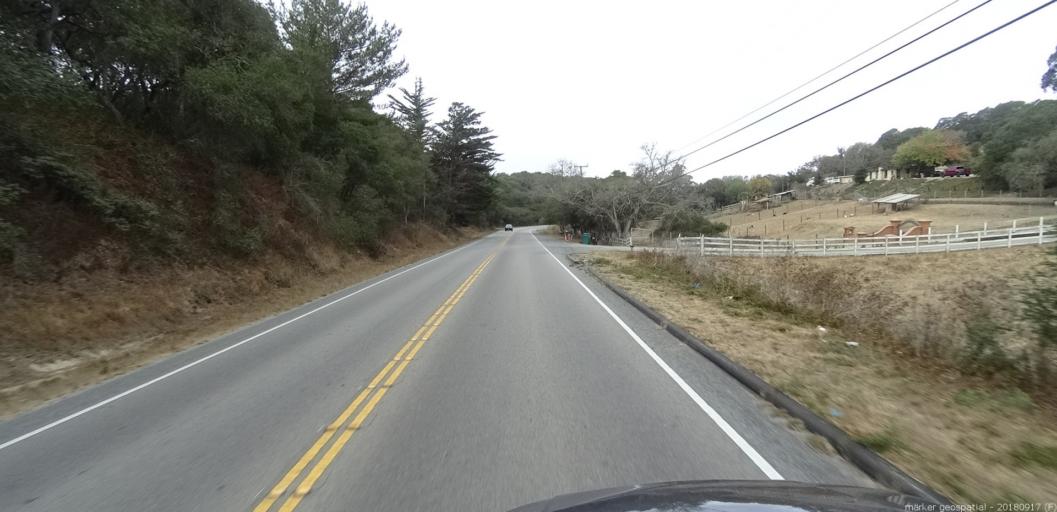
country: US
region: California
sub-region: Monterey County
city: Prunedale
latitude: 36.8011
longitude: -121.6866
